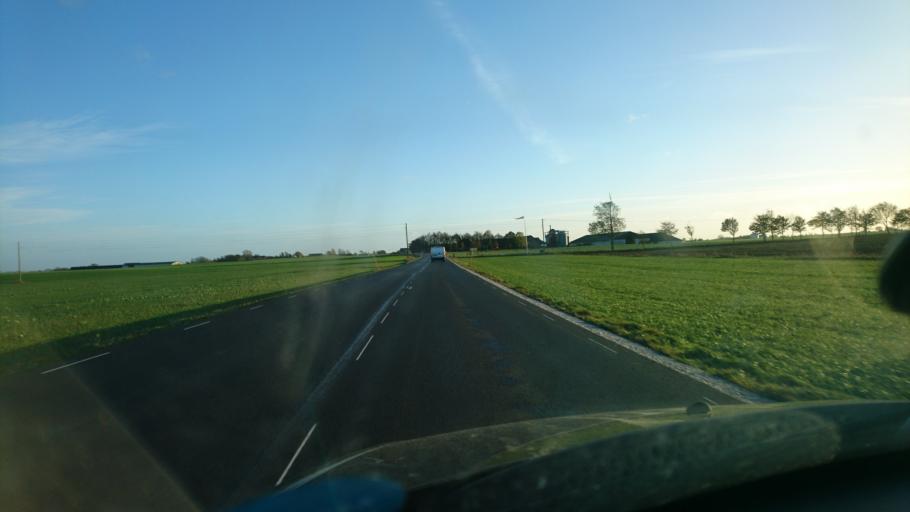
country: SE
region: Skane
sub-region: Tomelilla Kommun
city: Tomelilla
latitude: 55.5392
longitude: 14.1223
